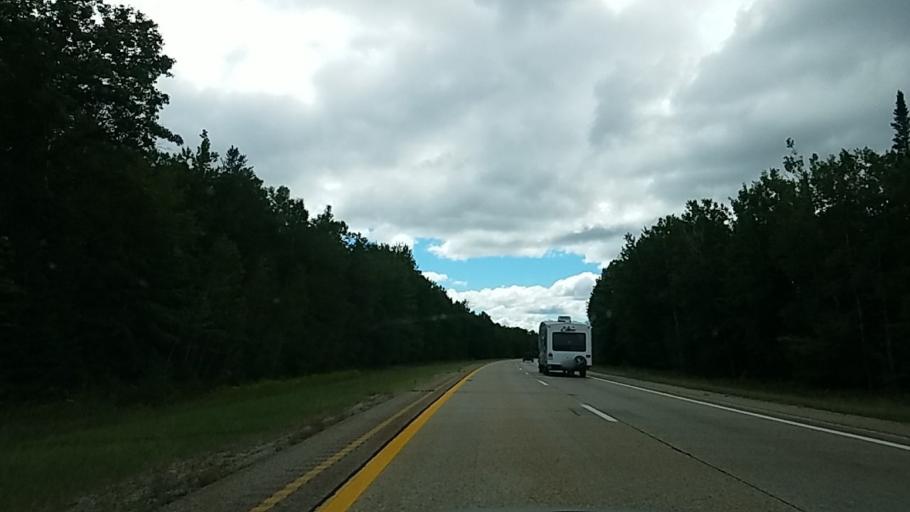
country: US
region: Michigan
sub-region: Ogemaw County
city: West Branch
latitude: 44.2024
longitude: -84.1902
